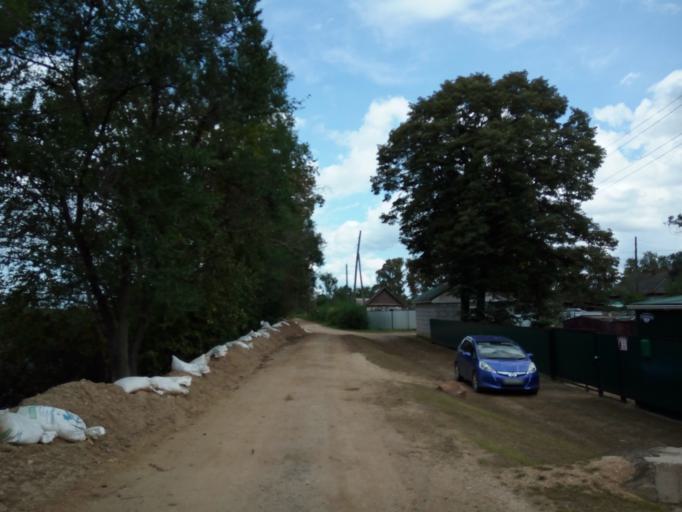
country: RU
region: Primorskiy
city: Dal'nerechensk
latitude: 45.9546
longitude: 133.8137
